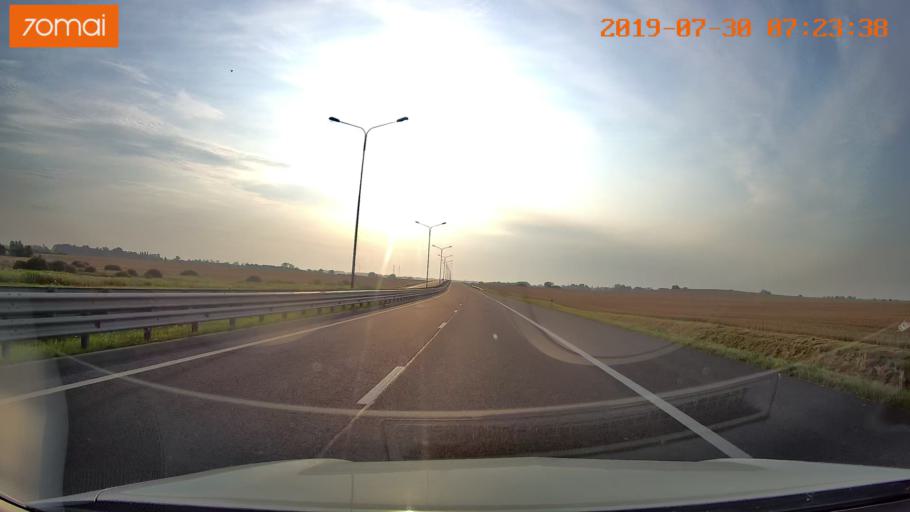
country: RU
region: Kaliningrad
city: Bol'shoe Isakovo
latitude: 54.6920
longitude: 20.7898
